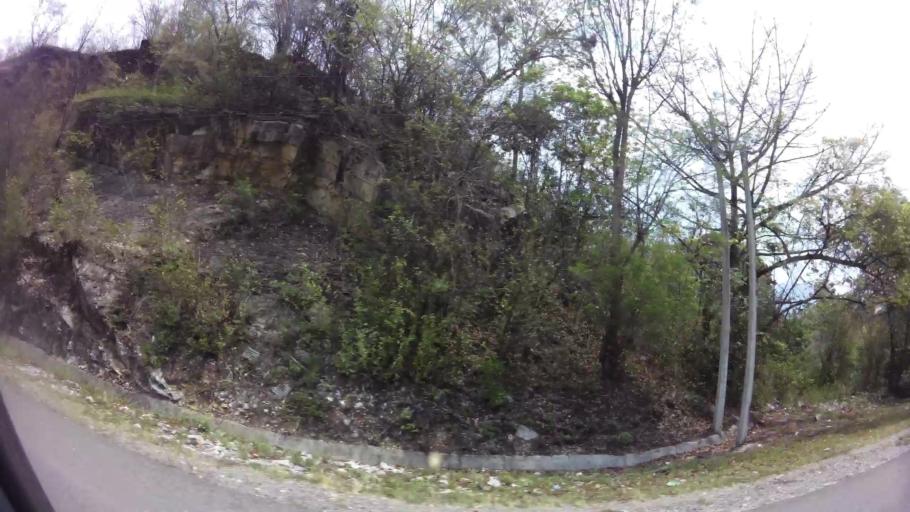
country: HN
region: Comayagua
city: Taulabe
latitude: 14.6948
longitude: -87.9511
